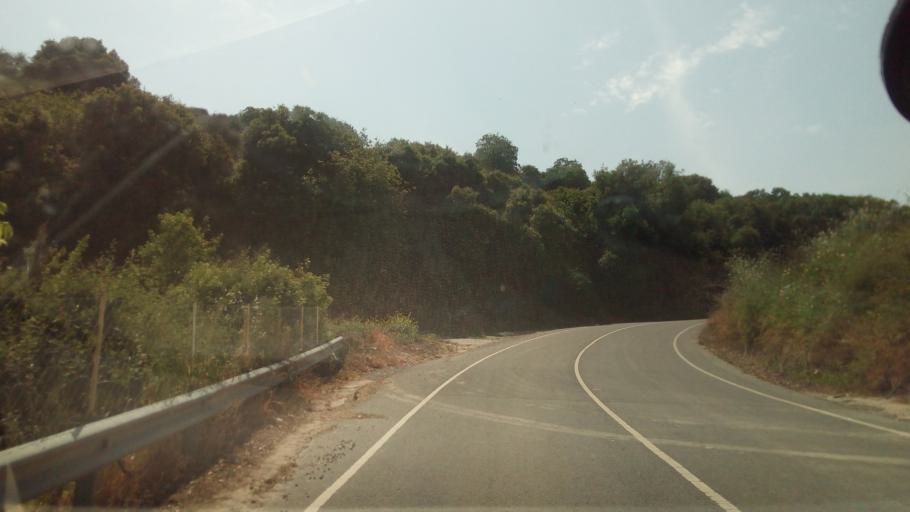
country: CY
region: Pafos
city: Polis
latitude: 34.9587
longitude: 32.4511
